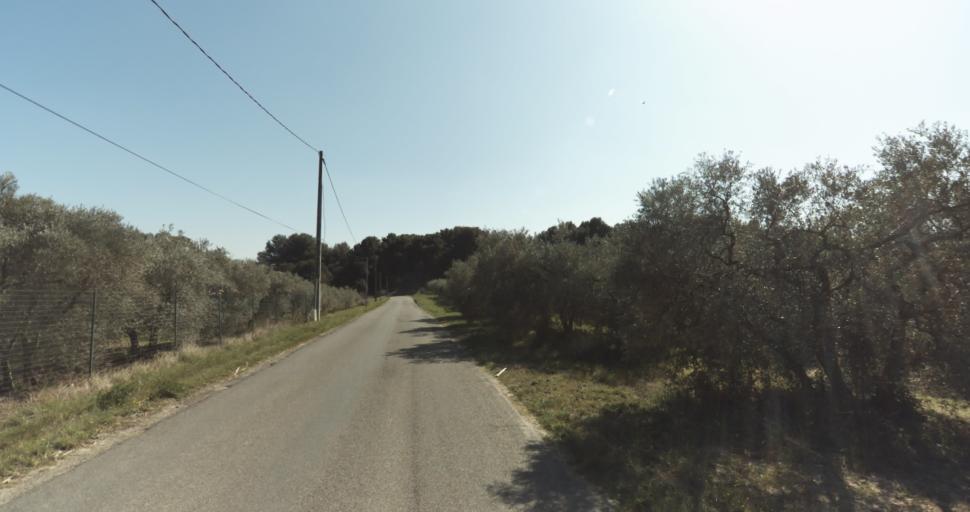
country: FR
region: Provence-Alpes-Cote d'Azur
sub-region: Departement des Bouches-du-Rhone
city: Pelissanne
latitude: 43.6512
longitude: 5.1801
